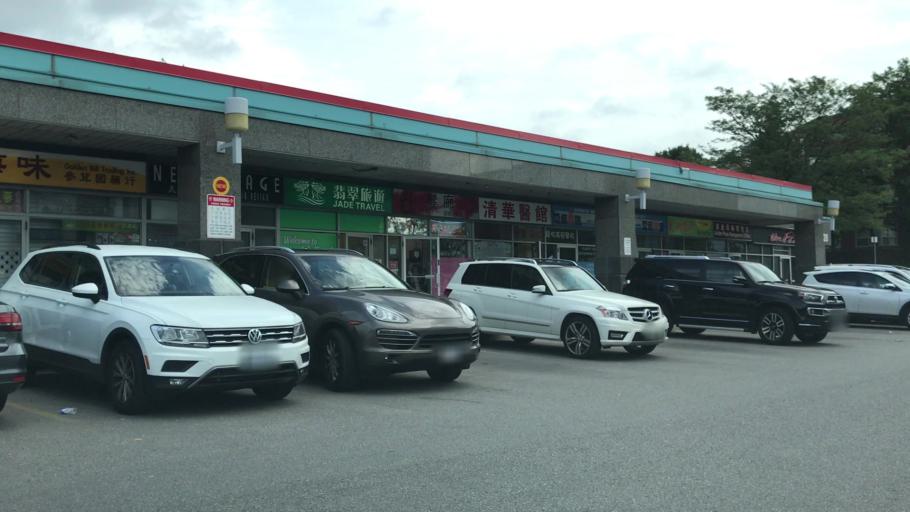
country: CA
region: Ontario
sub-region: York
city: Richmond Hill
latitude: 43.8413
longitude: -79.3995
